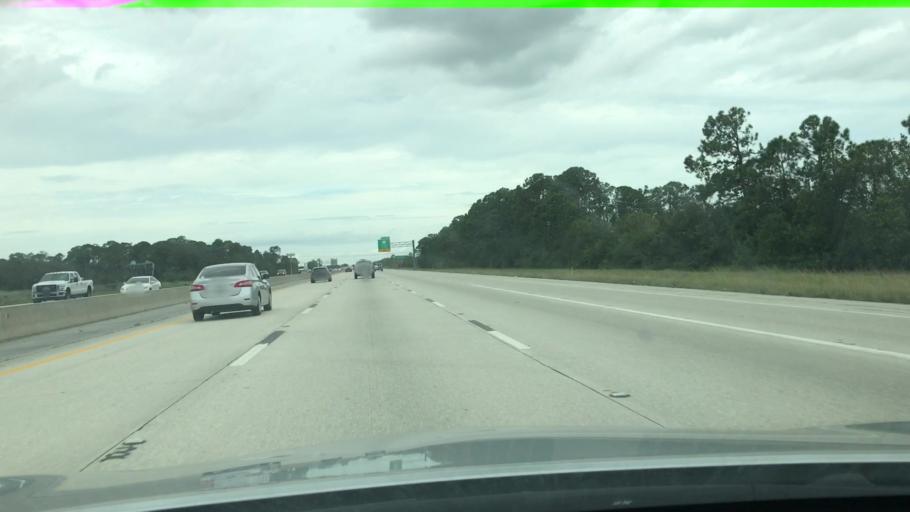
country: US
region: Florida
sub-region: Brevard County
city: Cocoa West
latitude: 28.3633
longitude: -80.7968
